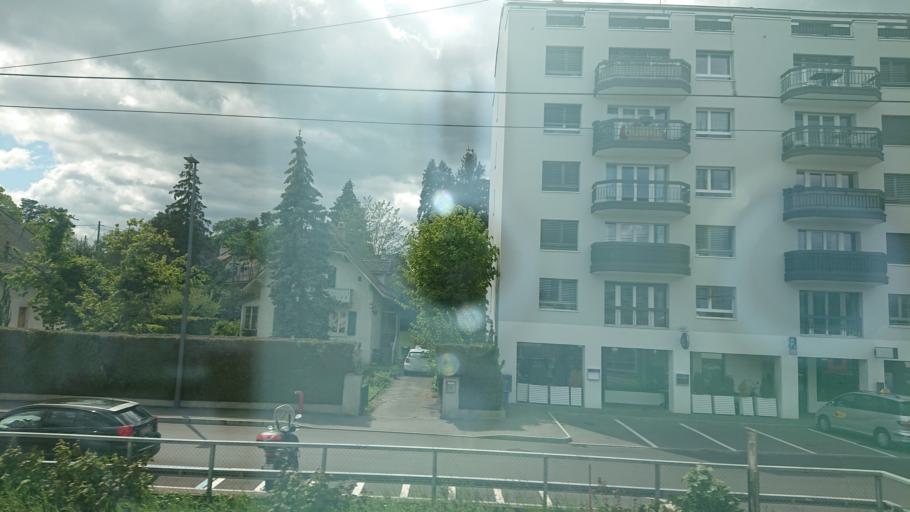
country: CH
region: Geneva
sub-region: Geneva
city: Versoix
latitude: 46.2817
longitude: 6.1643
